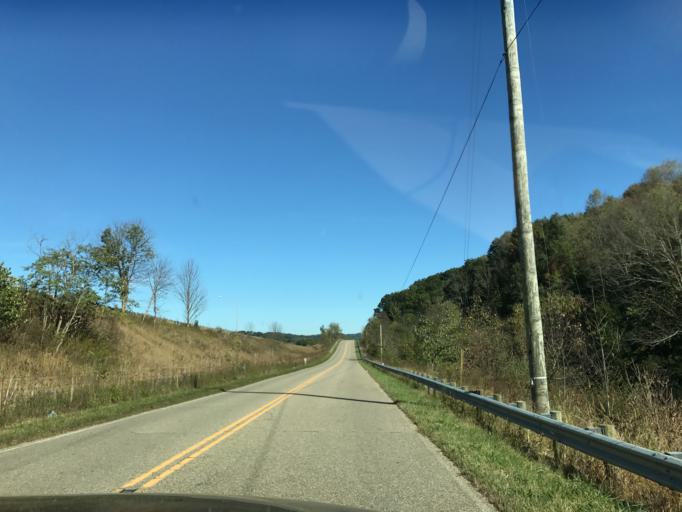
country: US
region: Ohio
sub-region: Guernsey County
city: Byesville
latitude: 40.0407
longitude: -81.3877
